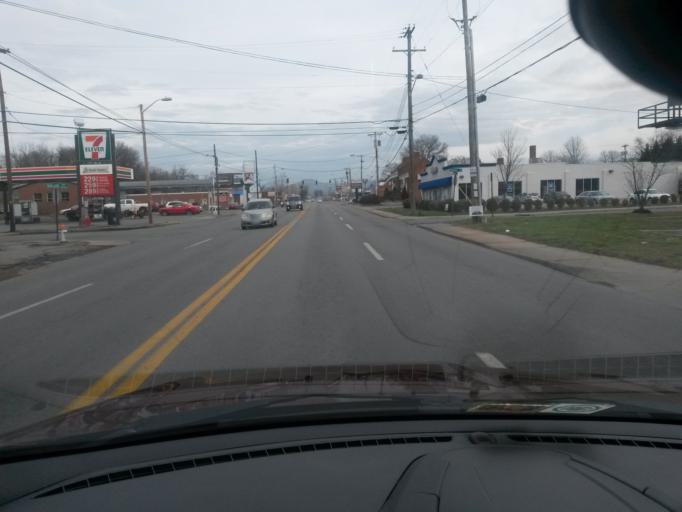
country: US
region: Virginia
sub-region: City of Roanoke
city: Roanoke
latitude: 37.3032
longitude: -79.9444
